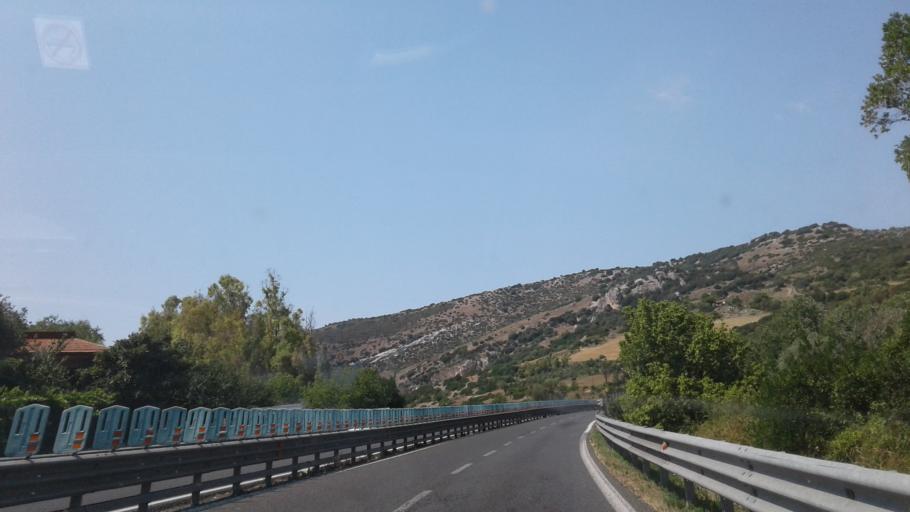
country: IT
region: Sardinia
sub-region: Provincia di Sassari
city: Muros
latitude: 40.6942
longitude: 8.6186
